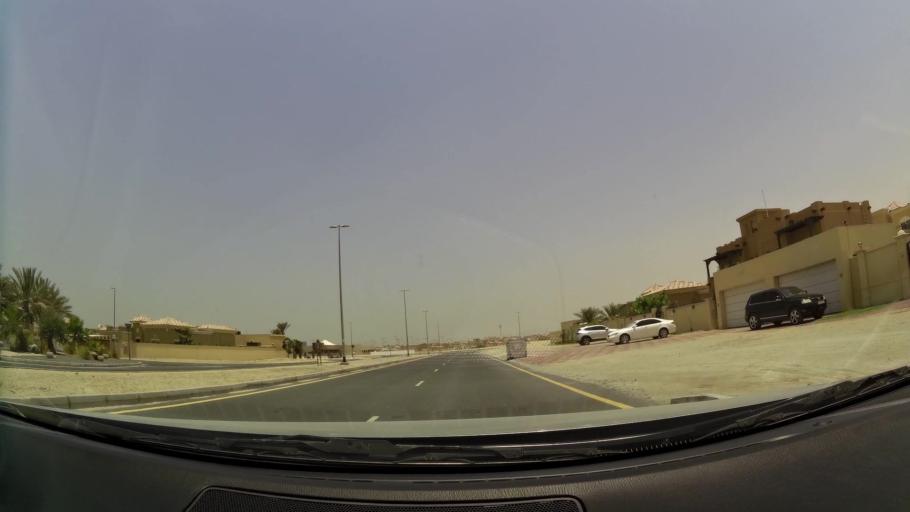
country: AE
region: Dubai
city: Dubai
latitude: 25.0839
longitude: 55.2408
